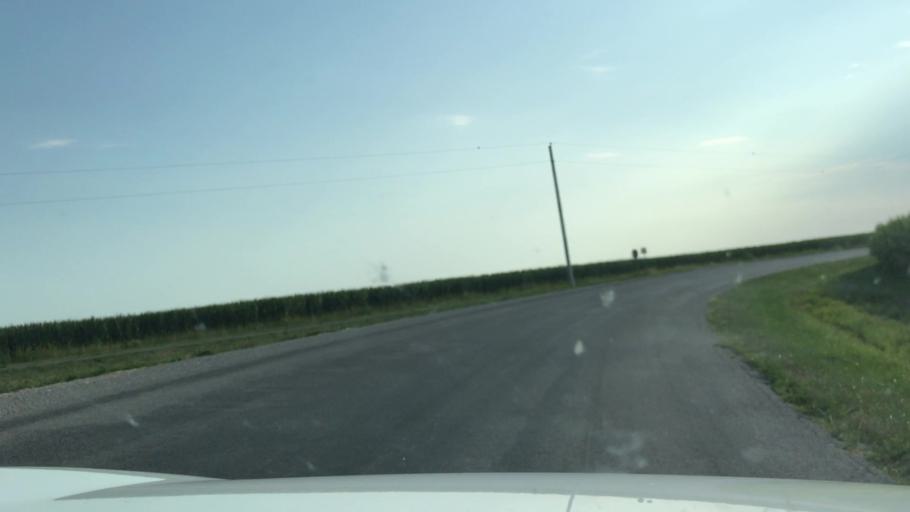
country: US
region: Illinois
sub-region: Washington County
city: Okawville
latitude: 38.4131
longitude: -89.4792
